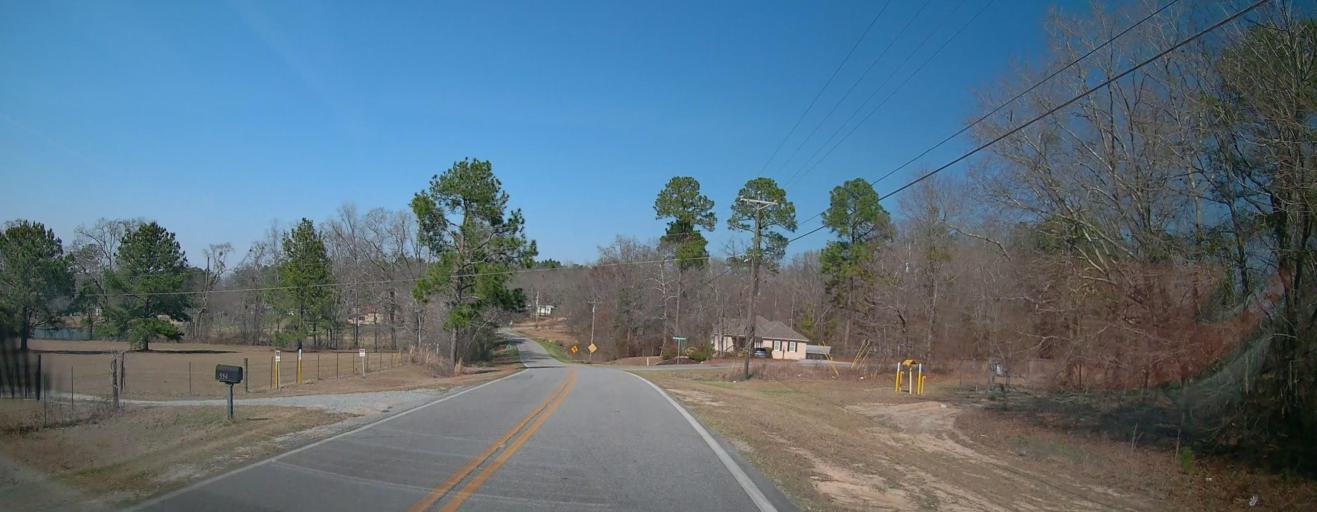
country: US
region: Georgia
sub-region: Bibb County
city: Macon
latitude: 32.8989
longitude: -83.5406
